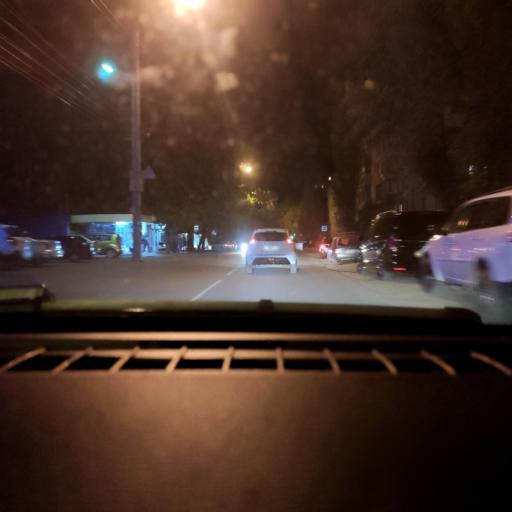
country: RU
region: Voronezj
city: Maslovka
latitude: 51.6347
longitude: 39.2748
